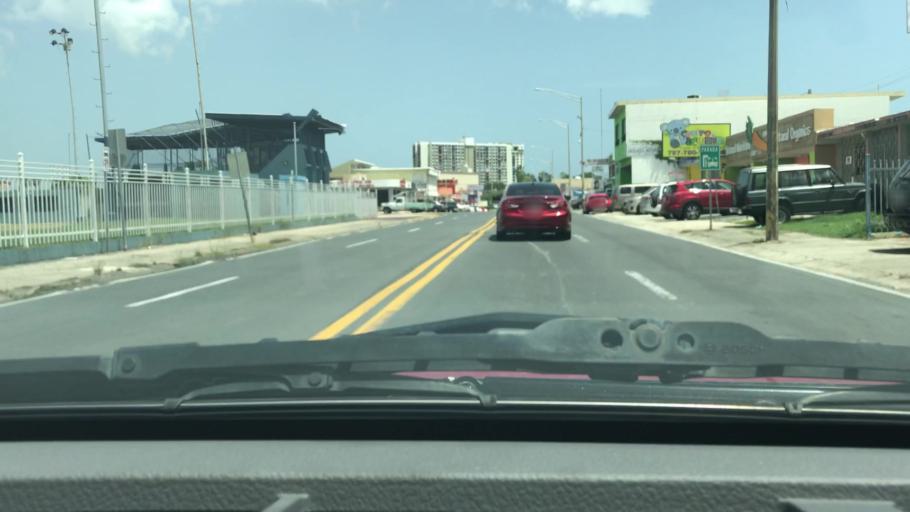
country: PR
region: Bayamon
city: Bayamon
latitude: 18.3914
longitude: -66.1417
